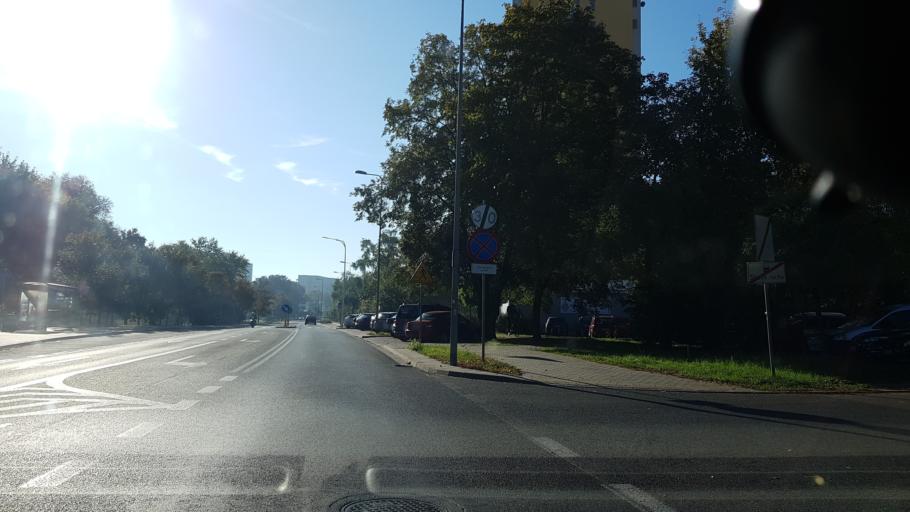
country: PL
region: Masovian Voivodeship
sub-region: Warszawa
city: Zoliborz
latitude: 52.2860
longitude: 20.9781
